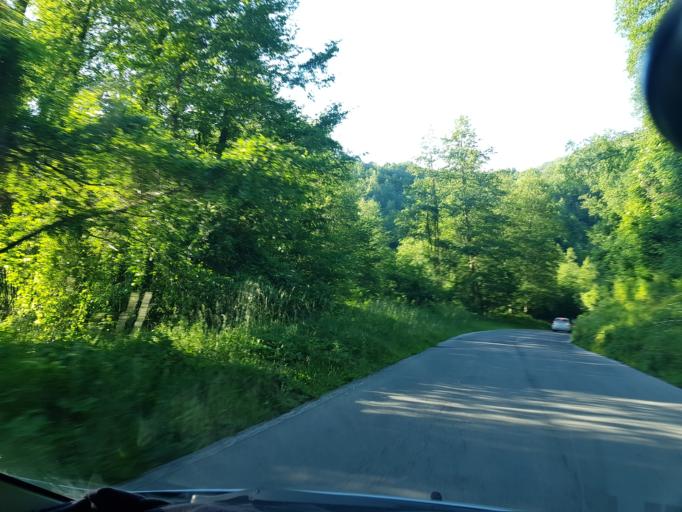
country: IT
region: Tuscany
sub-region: Provincia di Lucca
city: Minucciano
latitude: 44.1720
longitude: 10.2094
